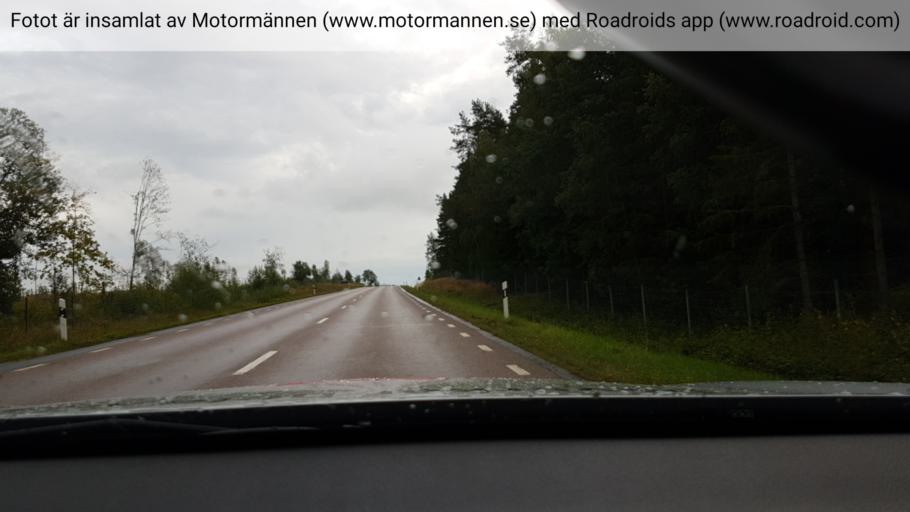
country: SE
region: Uppsala
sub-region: Tierps Kommun
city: Karlholmsbruk
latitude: 60.4378
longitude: 17.7889
